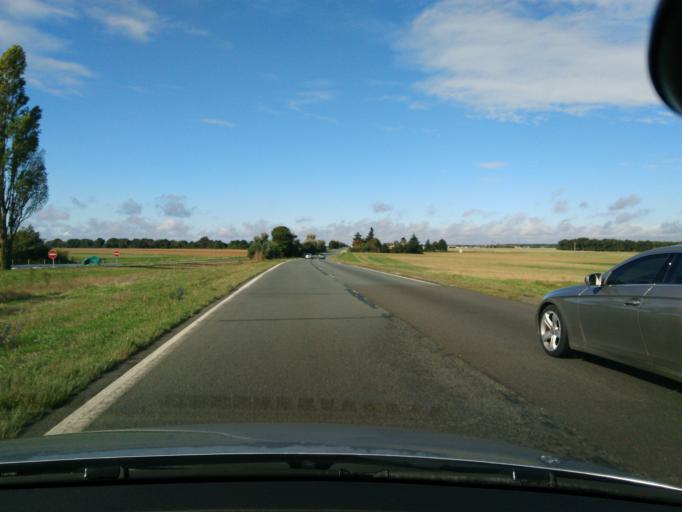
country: FR
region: Centre
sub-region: Departement d'Eure-et-Loir
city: Vert-en-Drouais
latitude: 48.7416
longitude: 1.3096
